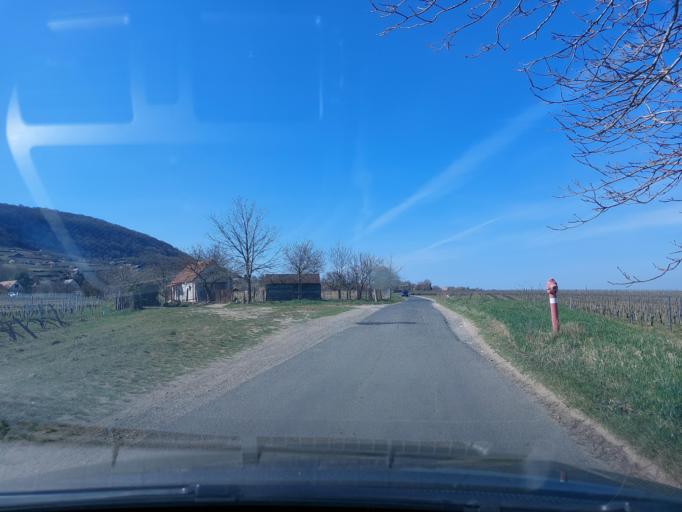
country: HU
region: Veszprem
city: Devecser
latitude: 47.1433
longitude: 17.3899
